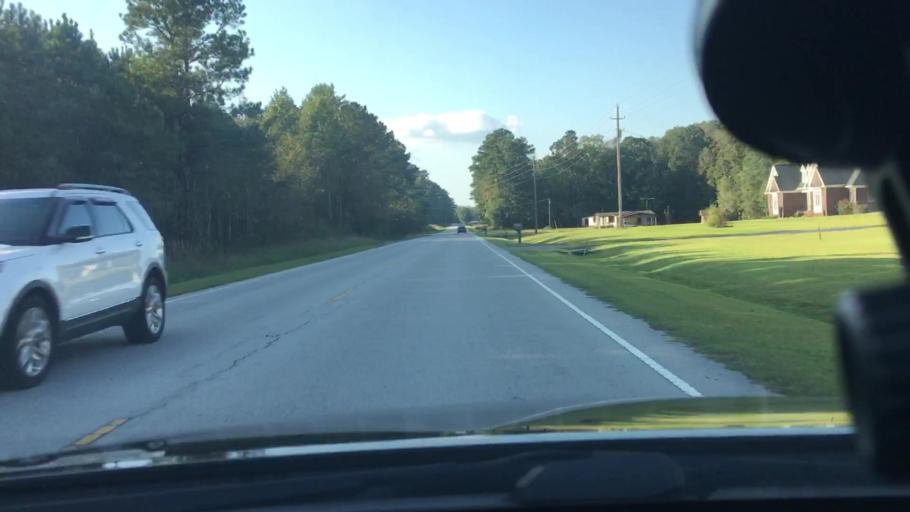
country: US
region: North Carolina
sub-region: Pitt County
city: Windsor
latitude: 35.4776
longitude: -77.2965
